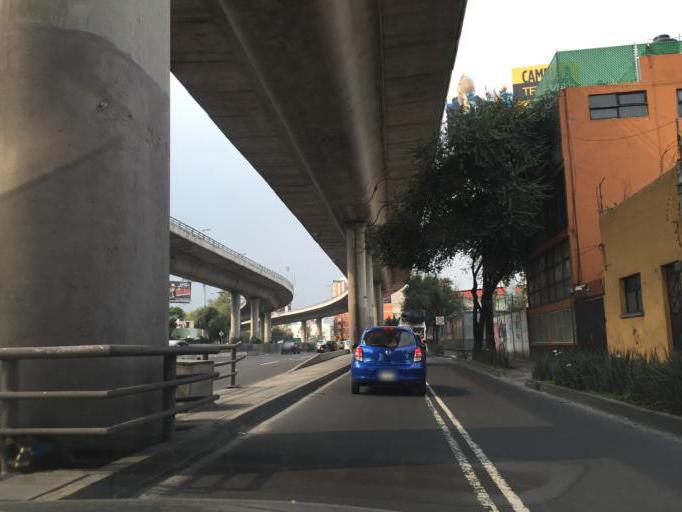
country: MX
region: Mexico City
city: Alvaro Obregon
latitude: 19.3655
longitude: -99.1907
